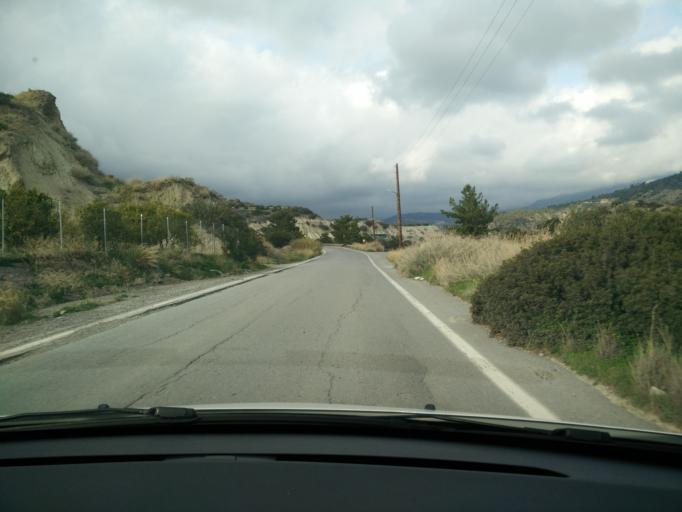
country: GR
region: Crete
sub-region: Nomos Lasithiou
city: Gra Liyia
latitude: 35.0137
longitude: 25.5835
